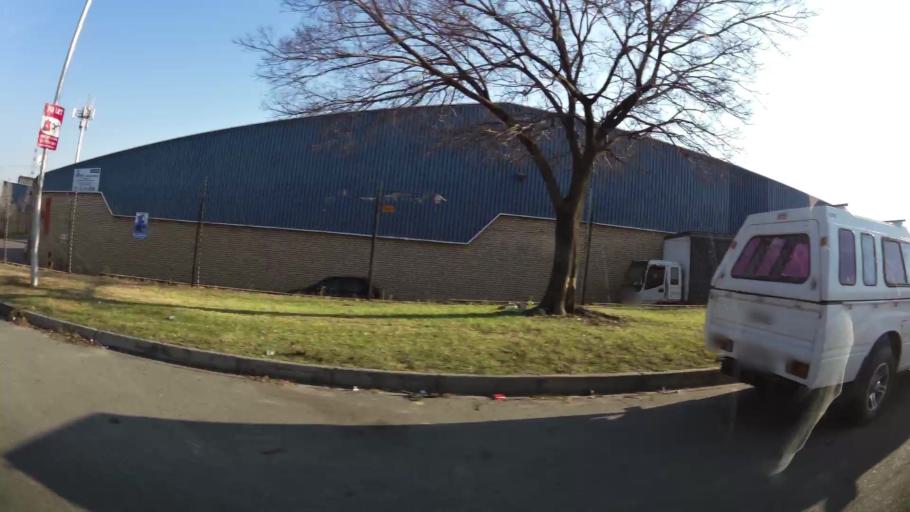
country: ZA
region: Gauteng
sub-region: City of Johannesburg Metropolitan Municipality
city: Modderfontein
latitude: -26.1466
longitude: 28.1846
